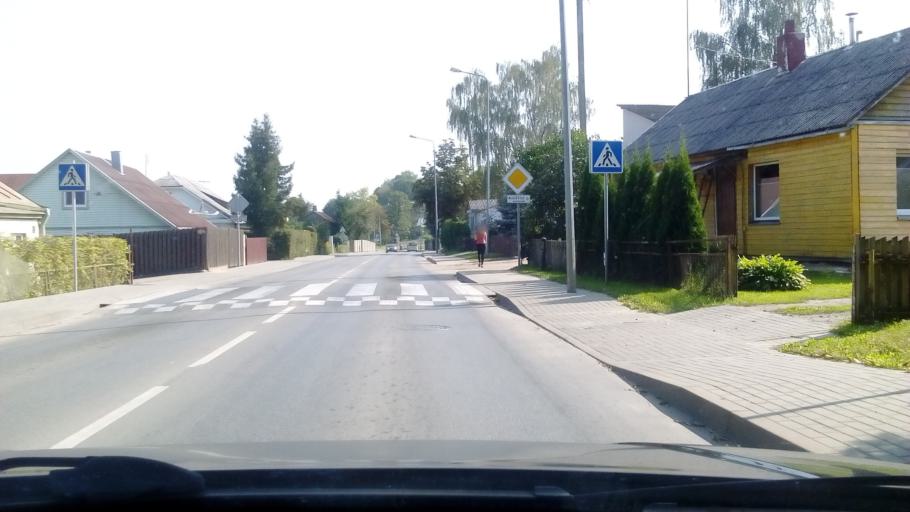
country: LT
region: Alytaus apskritis
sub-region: Alytus
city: Alytus
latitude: 54.4018
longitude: 24.0428
